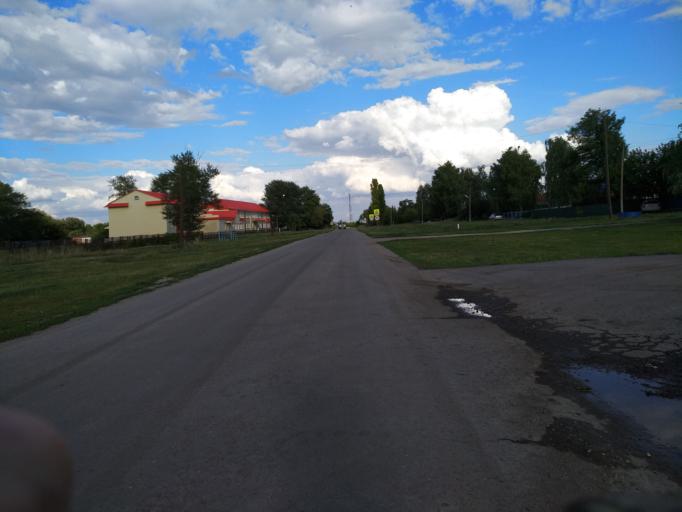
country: RU
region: Lipetsk
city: Dobrinka
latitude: 52.0386
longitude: 40.5419
